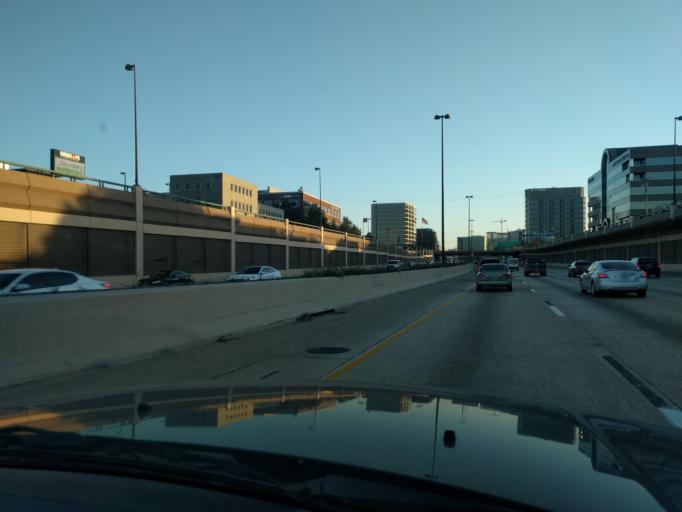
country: US
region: Texas
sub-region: Dallas County
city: Highland Park
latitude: 32.8183
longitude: -96.7881
